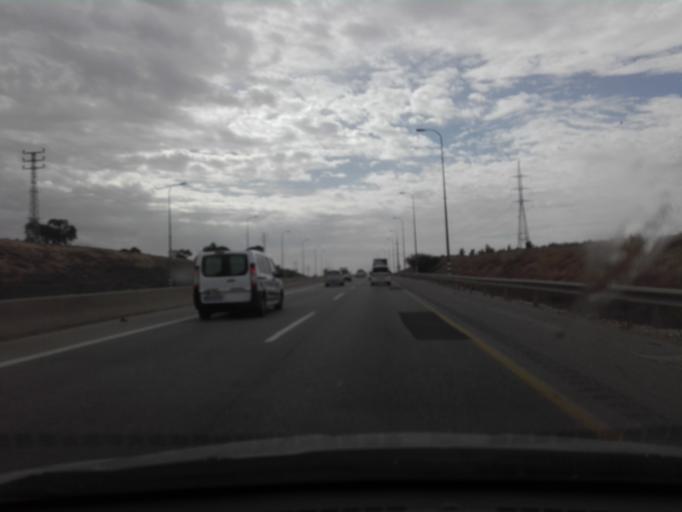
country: IL
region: Southern District
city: Lehavim
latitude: 31.3490
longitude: 34.7916
